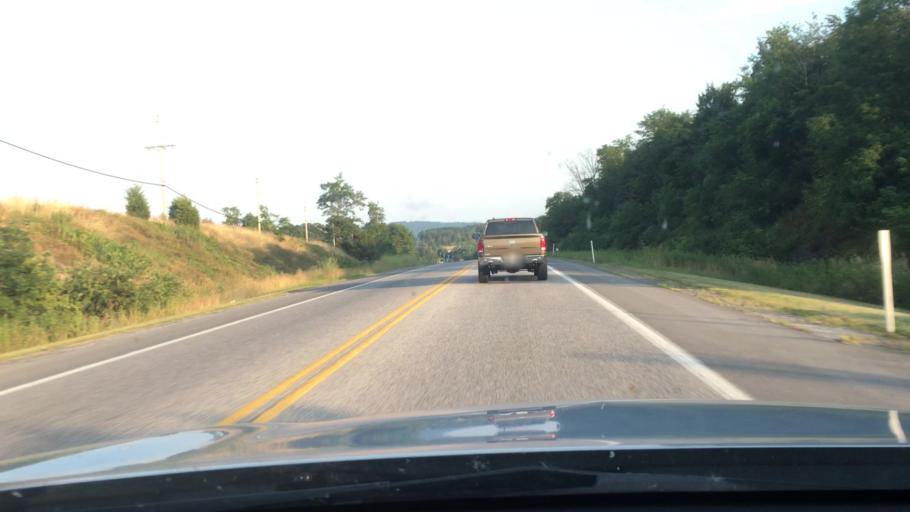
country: US
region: Pennsylvania
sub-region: York County
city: Dover
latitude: 40.0714
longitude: -76.9235
